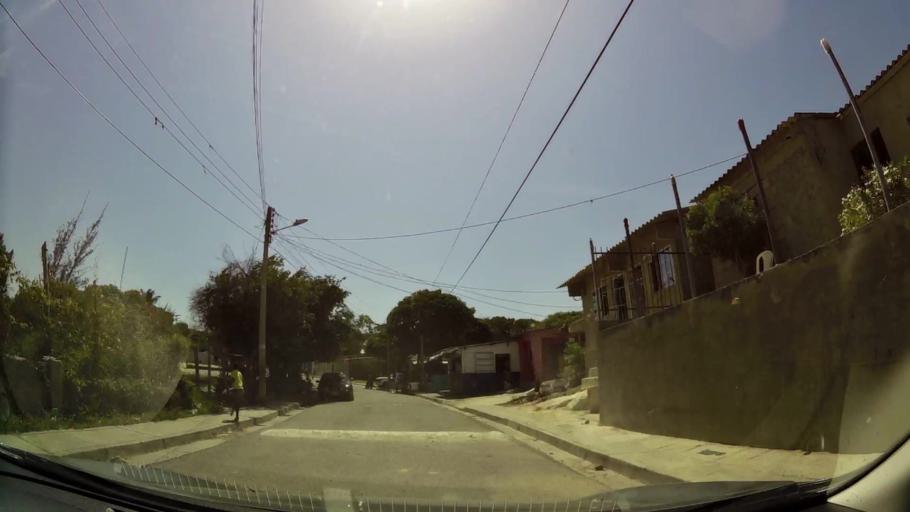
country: CO
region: Bolivar
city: Cartagena
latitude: 10.4279
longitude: -75.5263
